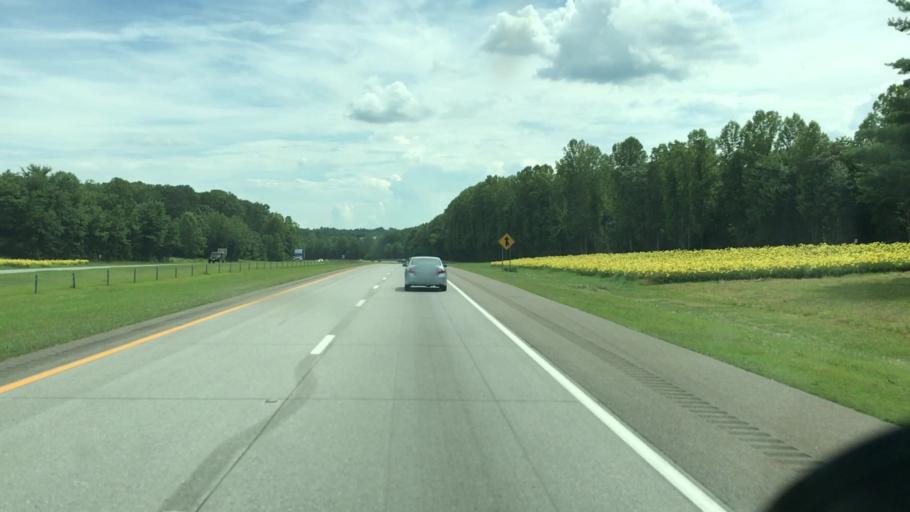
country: US
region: North Carolina
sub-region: Surry County
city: Elkin
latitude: 36.2790
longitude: -80.8227
